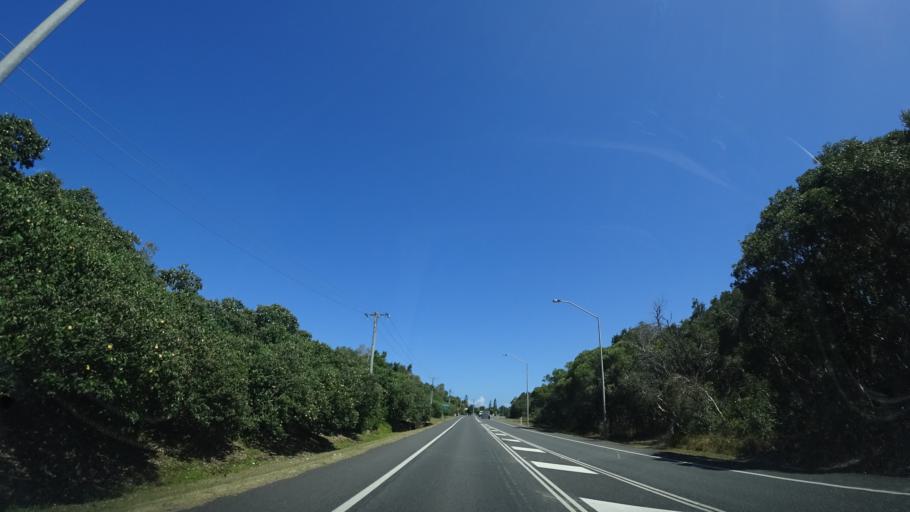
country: AU
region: Queensland
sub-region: Sunshine Coast
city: Coolum Beach
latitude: -26.5782
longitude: 153.0918
